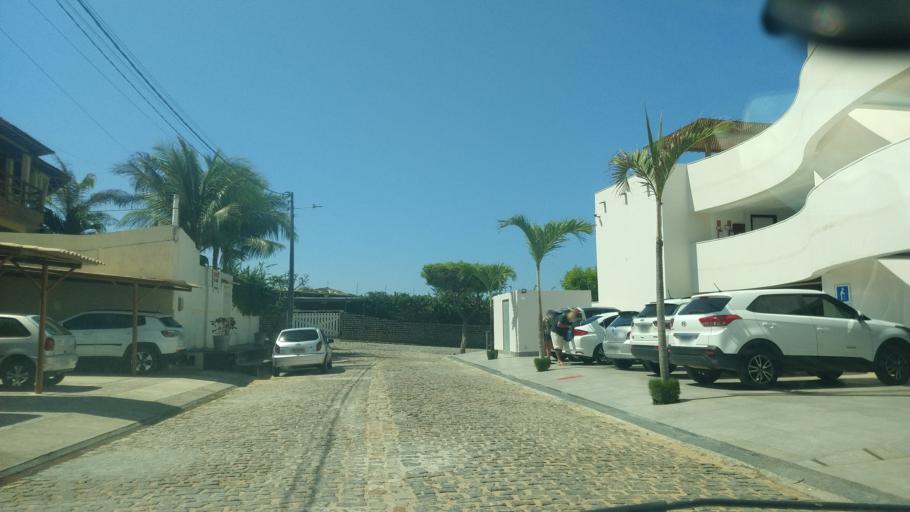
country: BR
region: Rio Grande do Norte
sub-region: Parnamirim
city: Parnamirim
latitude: -5.9475
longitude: -35.1542
